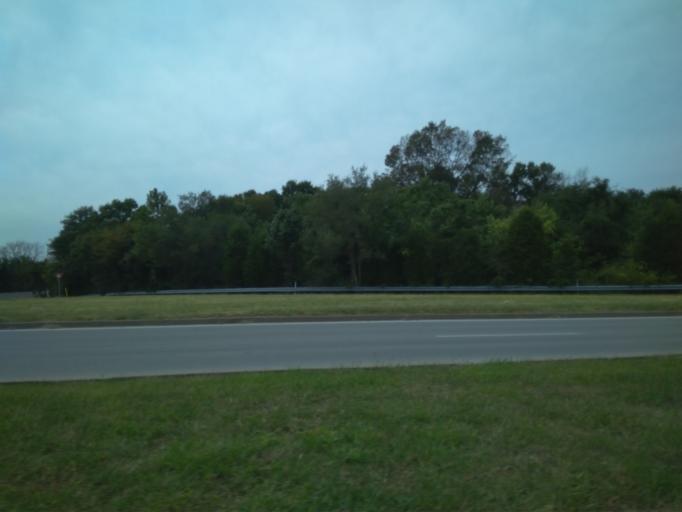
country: US
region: Kentucky
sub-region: Jefferson County
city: Anchorage
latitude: 38.2722
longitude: -85.5630
